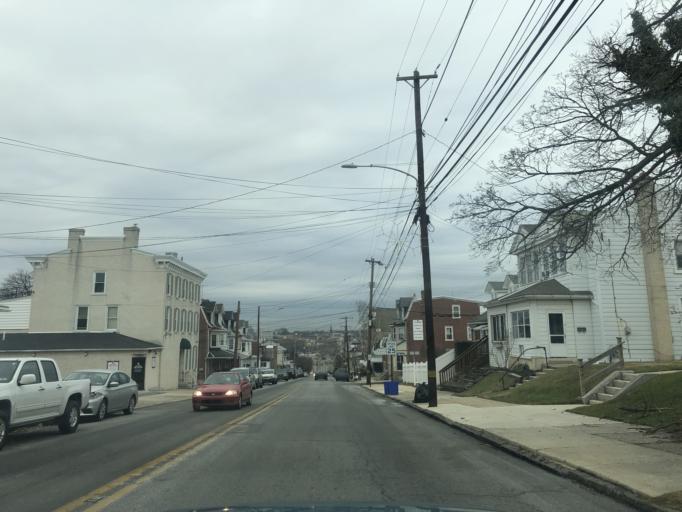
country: US
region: Pennsylvania
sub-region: Montgomery County
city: Bridgeport
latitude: 40.1031
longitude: -75.3484
